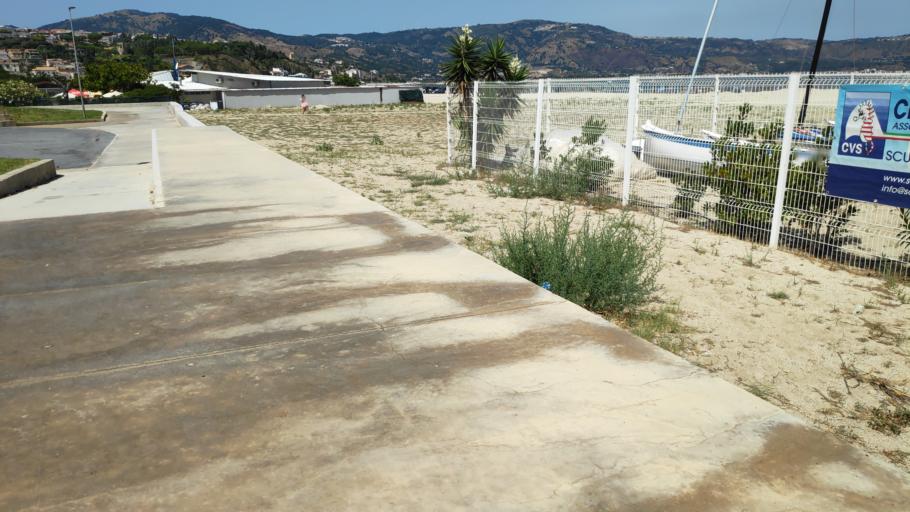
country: IT
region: Calabria
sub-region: Provincia di Catanzaro
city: Soverato Marina
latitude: 38.6902
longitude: 16.5537
